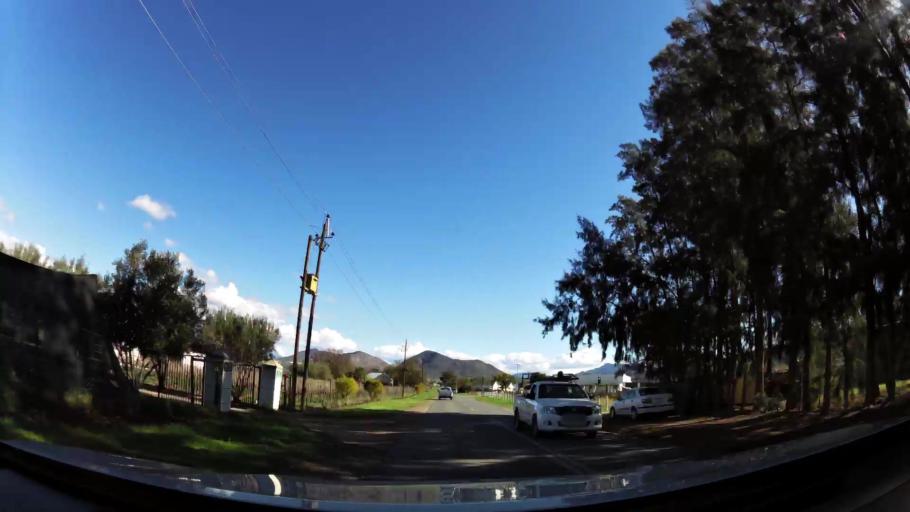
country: ZA
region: Western Cape
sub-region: Cape Winelands District Municipality
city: Ashton
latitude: -33.8064
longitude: 19.8634
